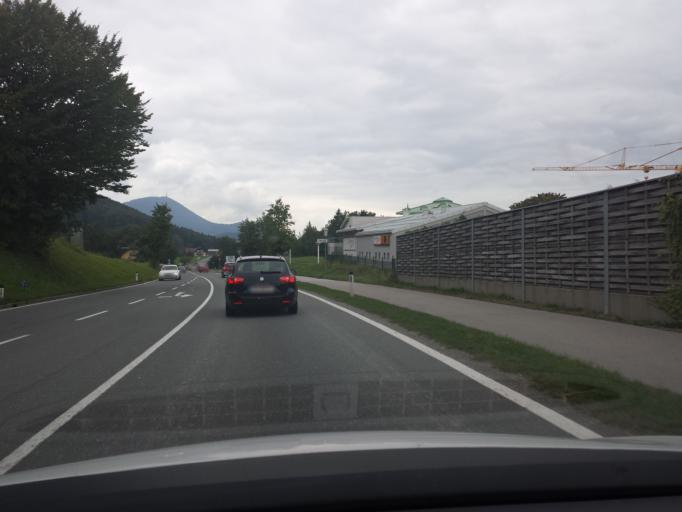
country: AT
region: Salzburg
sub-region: Politischer Bezirk Salzburg-Umgebung
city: Hof bei Salzburg
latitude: 47.8201
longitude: 13.2072
